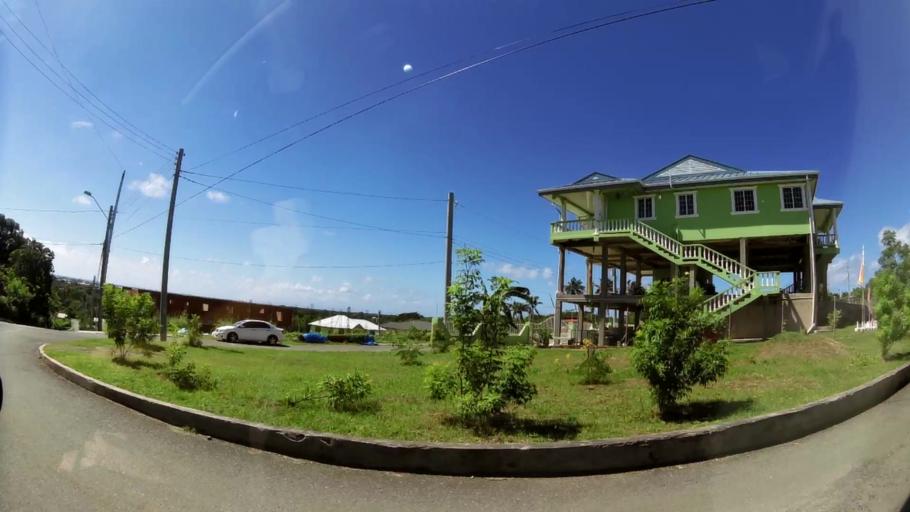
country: TT
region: Tobago
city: Scarborough
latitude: 11.1712
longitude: -60.7749
